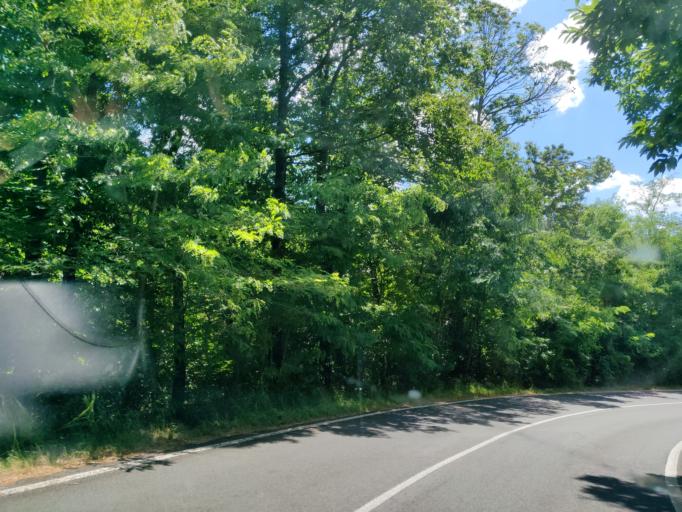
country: IT
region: Tuscany
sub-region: Provincia di Siena
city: Abbadia San Salvatore
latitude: 42.8871
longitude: 11.6570
